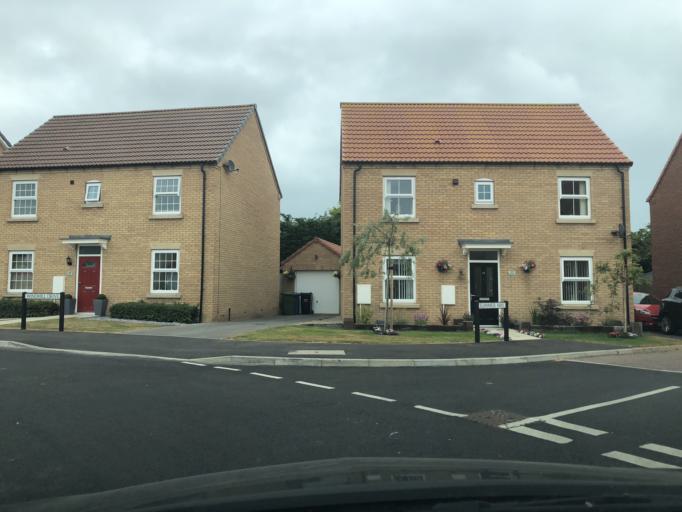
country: GB
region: England
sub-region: North Yorkshire
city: Filey
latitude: 54.2052
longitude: -0.3002
